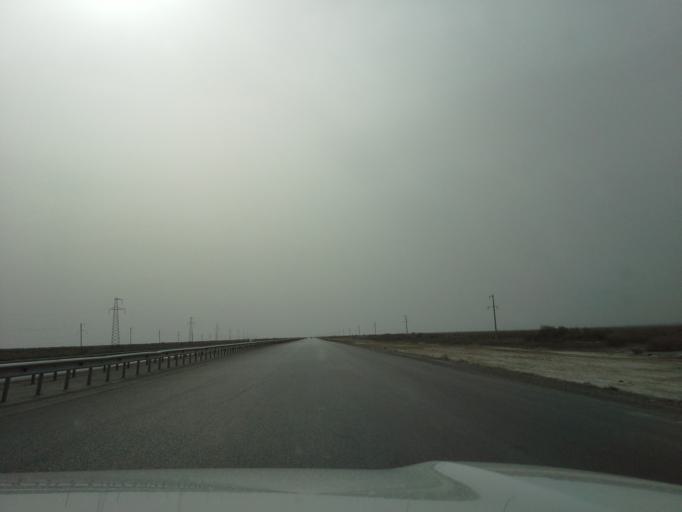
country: TM
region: Ahal
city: Kaka
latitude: 37.5167
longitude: 59.4342
